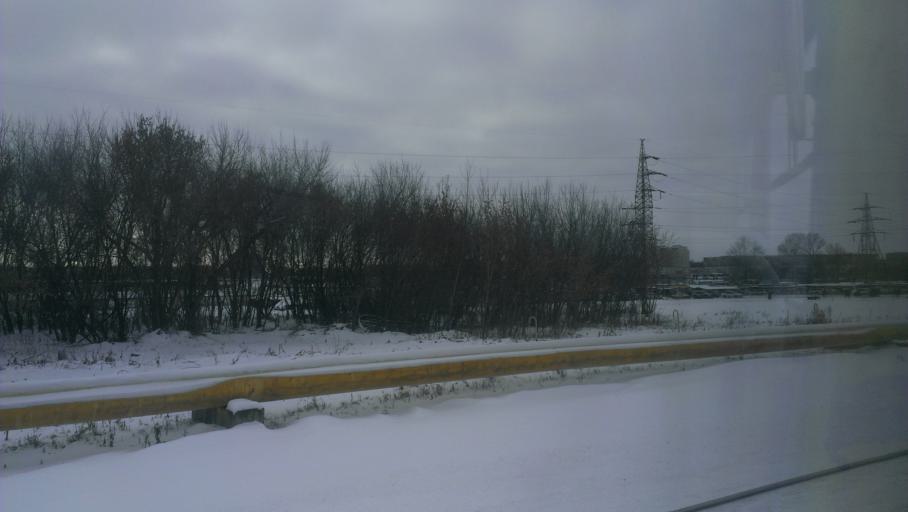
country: RU
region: Altai Krai
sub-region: Gorod Barnaulskiy
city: Barnaul
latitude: 53.3872
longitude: 83.6935
